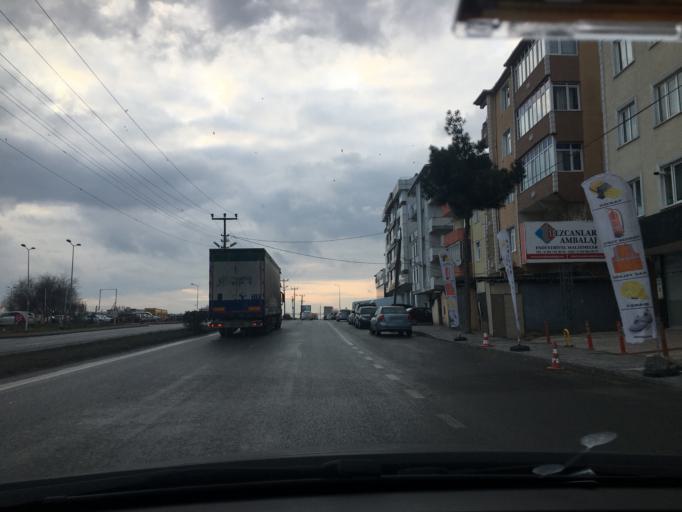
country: TR
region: Tekirdag
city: Cerkezkoey
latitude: 41.2794
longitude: 27.9845
